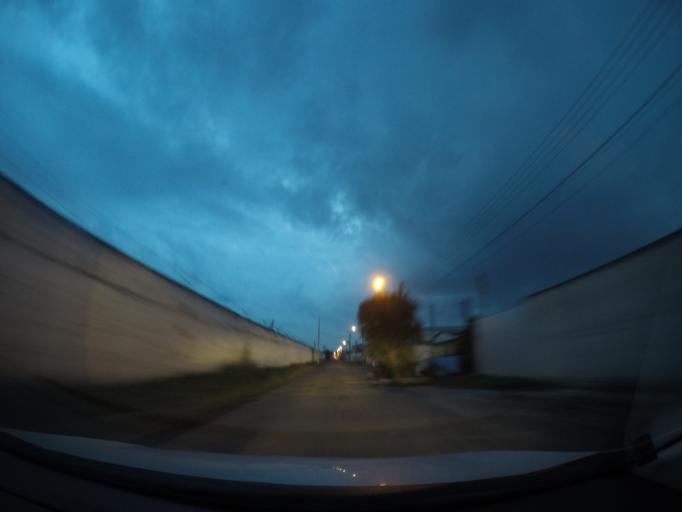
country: BR
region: Parana
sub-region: Sao Jose Dos Pinhais
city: Sao Jose dos Pinhais
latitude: -25.5198
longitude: -49.2237
